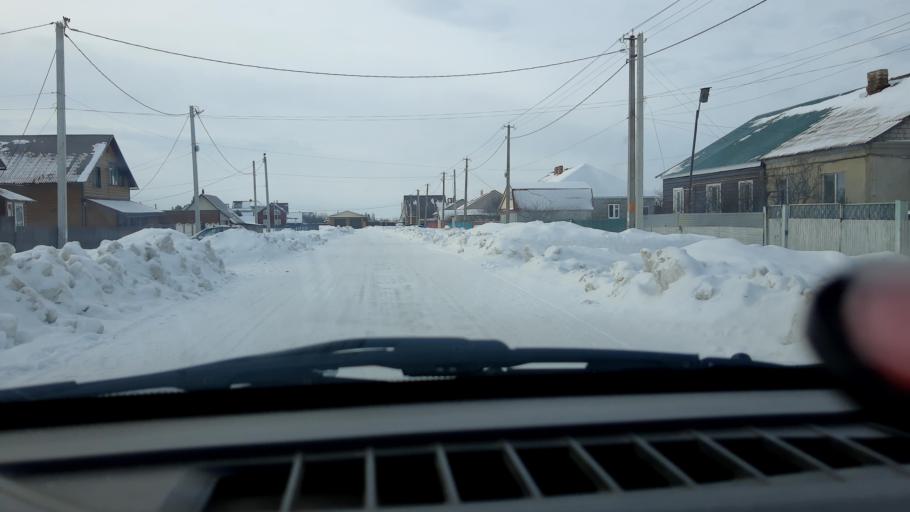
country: RU
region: Bashkortostan
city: Kabakovo
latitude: 54.6010
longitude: 56.1874
